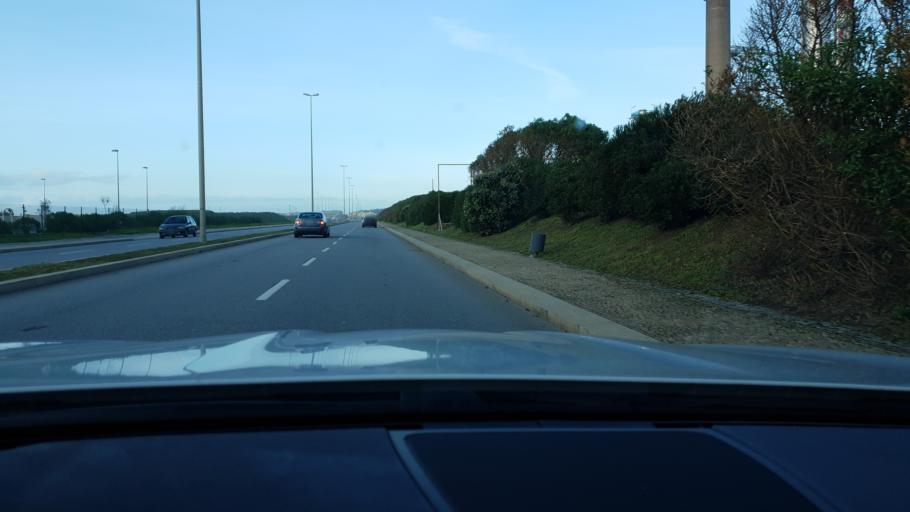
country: PT
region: Porto
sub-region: Matosinhos
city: Leca da Palmeira
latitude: 41.2119
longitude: -8.7133
